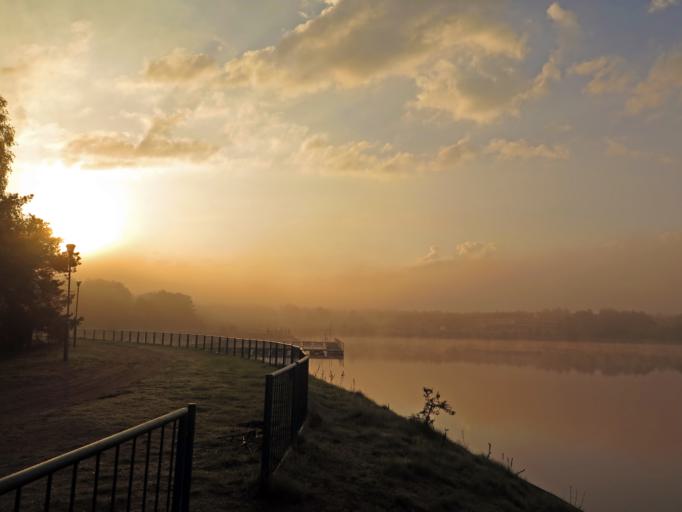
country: PL
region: Lodz Voivodeship
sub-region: Powiat belchatowski
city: Kleszczow
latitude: 51.2794
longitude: 19.3585
